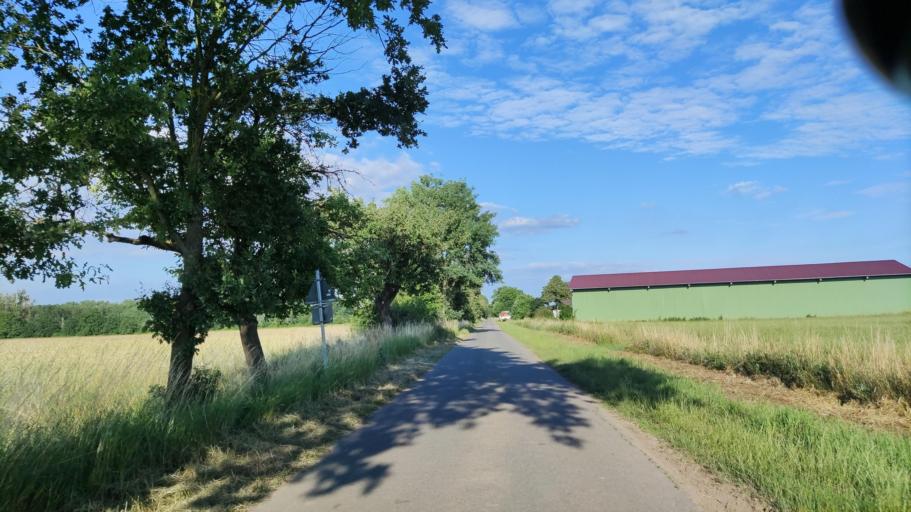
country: DE
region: Brandenburg
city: Lanz
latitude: 53.0410
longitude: 11.5408
